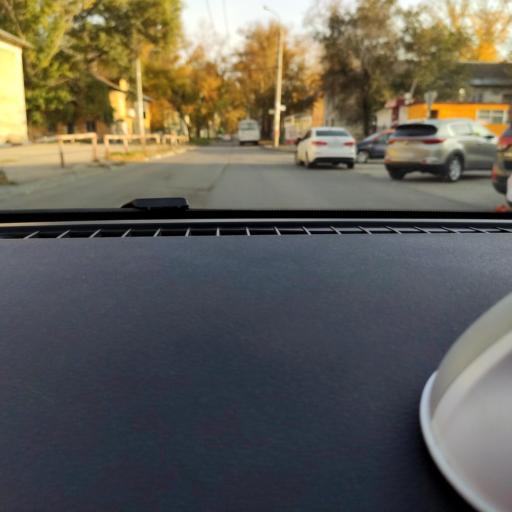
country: RU
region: Samara
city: Samara
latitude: 53.2204
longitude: 50.2511
